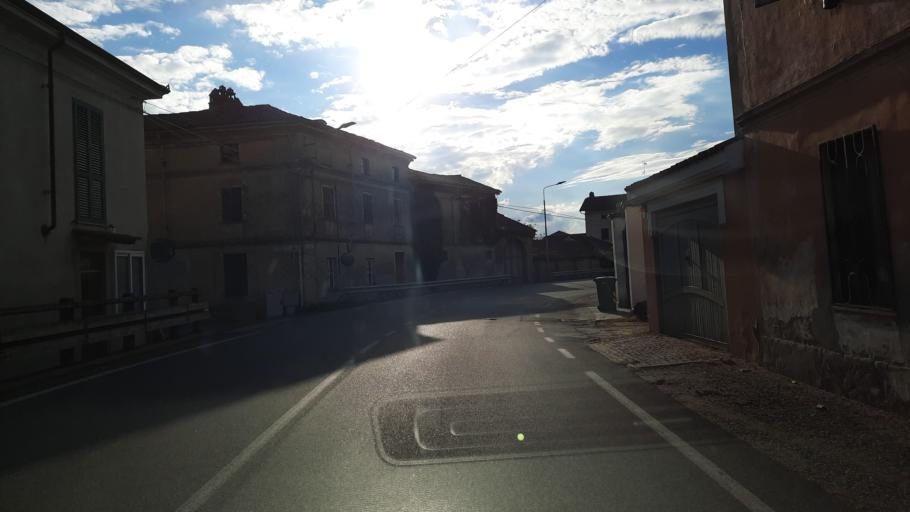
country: IT
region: Piedmont
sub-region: Provincia di Vercelli
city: Palazzolo Vercellese
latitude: 45.1861
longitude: 8.2315
